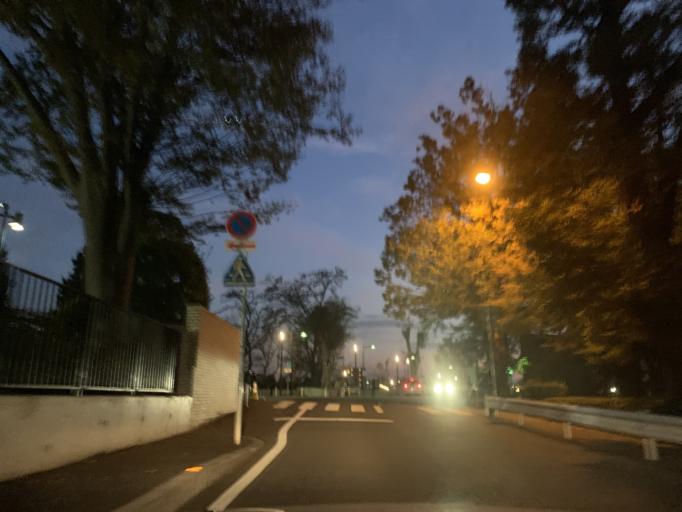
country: JP
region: Chiba
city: Noda
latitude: 35.9176
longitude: 139.9064
